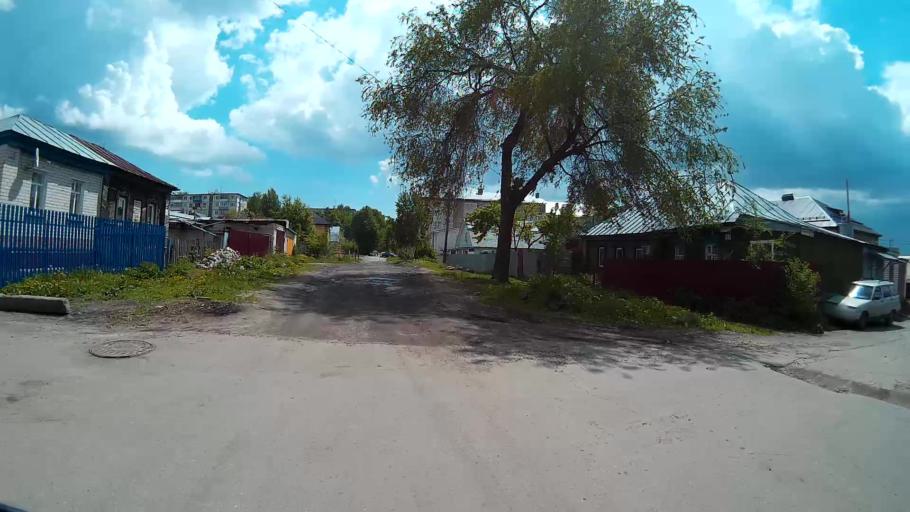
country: RU
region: Ulyanovsk
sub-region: Ulyanovskiy Rayon
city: Ulyanovsk
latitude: 54.3431
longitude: 48.3674
